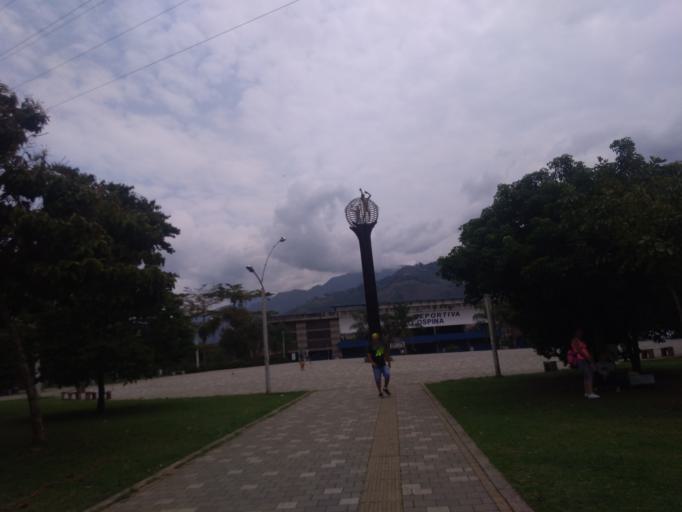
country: CO
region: Antioquia
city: Bello
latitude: 6.3351
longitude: -75.5481
